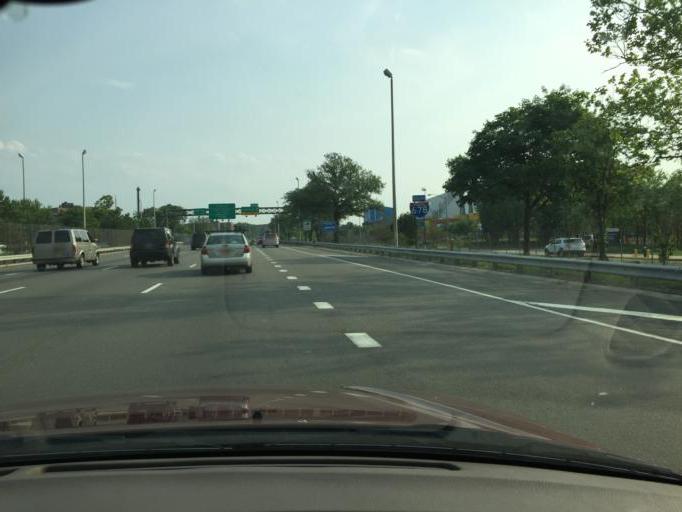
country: US
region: New York
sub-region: Nassau County
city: East Atlantic Beach
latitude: 40.7774
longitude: -73.8277
